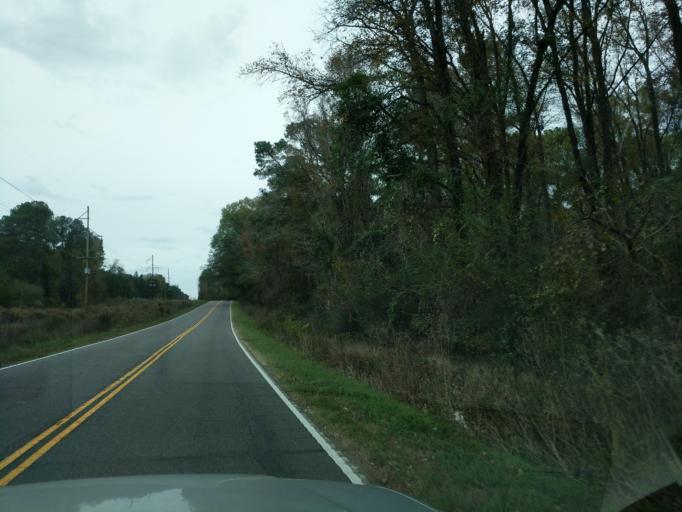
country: US
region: South Carolina
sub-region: Lexington County
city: Batesburg
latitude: 33.9471
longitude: -81.6262
